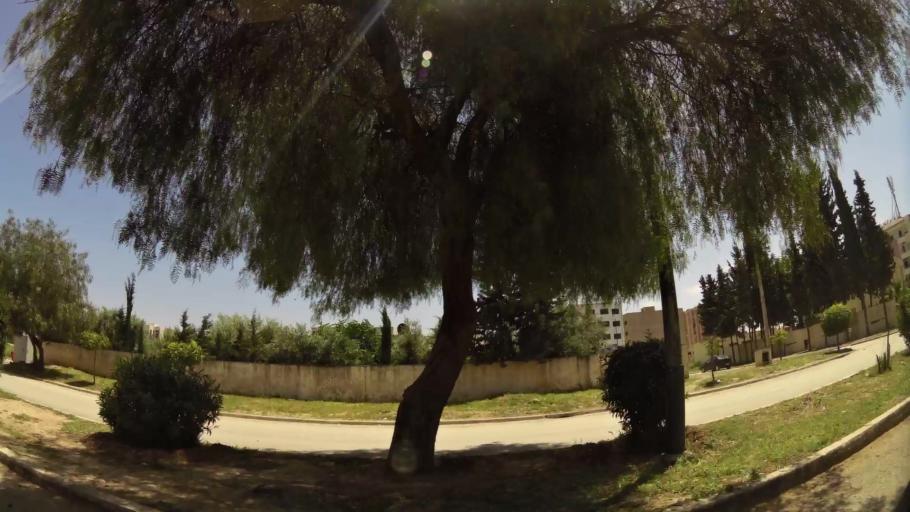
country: MA
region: Fes-Boulemane
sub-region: Fes
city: Fes
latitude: 34.0290
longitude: -5.0431
